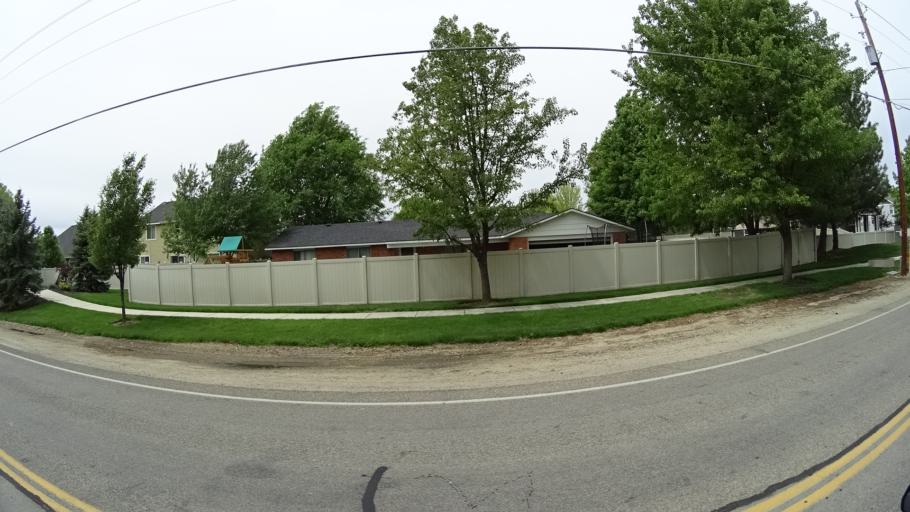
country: US
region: Idaho
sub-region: Ada County
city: Meridian
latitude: 43.5717
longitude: -116.3746
